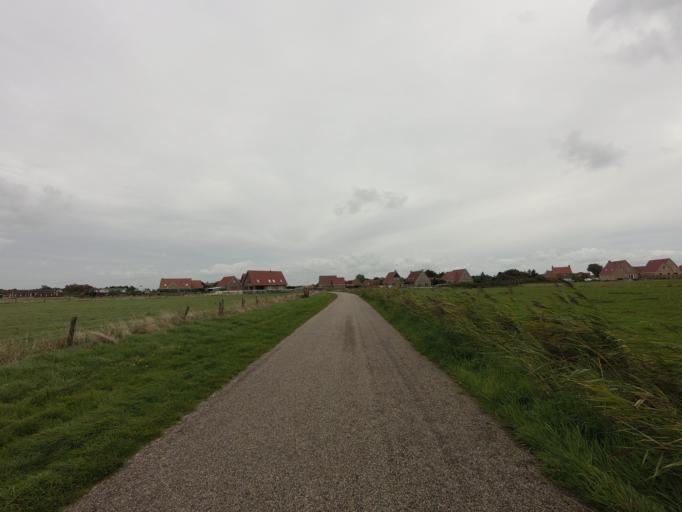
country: NL
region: Friesland
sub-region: Gemeente Ameland
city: Nes
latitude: 53.4518
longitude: 5.7976
